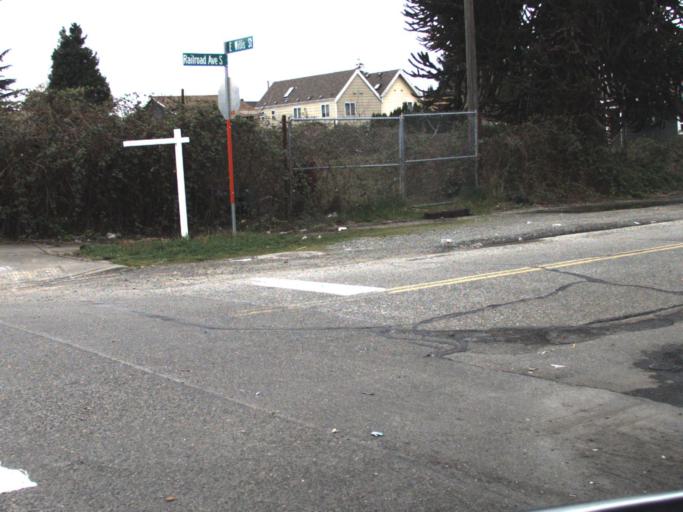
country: US
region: Washington
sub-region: King County
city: Kent
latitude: 47.3778
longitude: -122.2322
